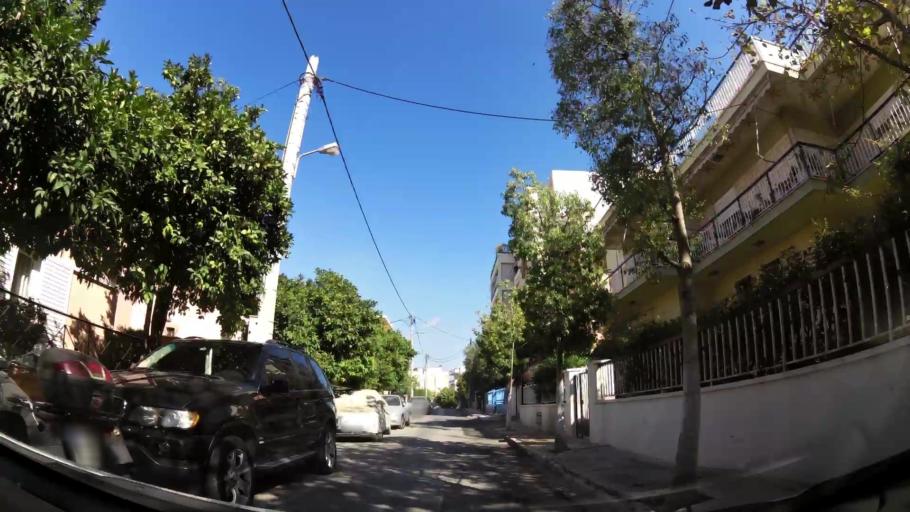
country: GR
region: Attica
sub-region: Nomarchia Athinas
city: Metamorfosi
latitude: 38.0664
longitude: 23.7648
